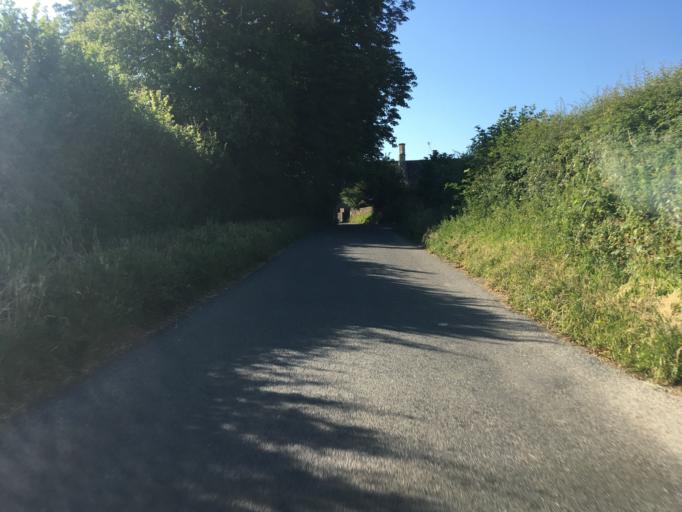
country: GB
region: England
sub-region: South Gloucestershire
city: Hinton
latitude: 51.4798
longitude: -2.3805
